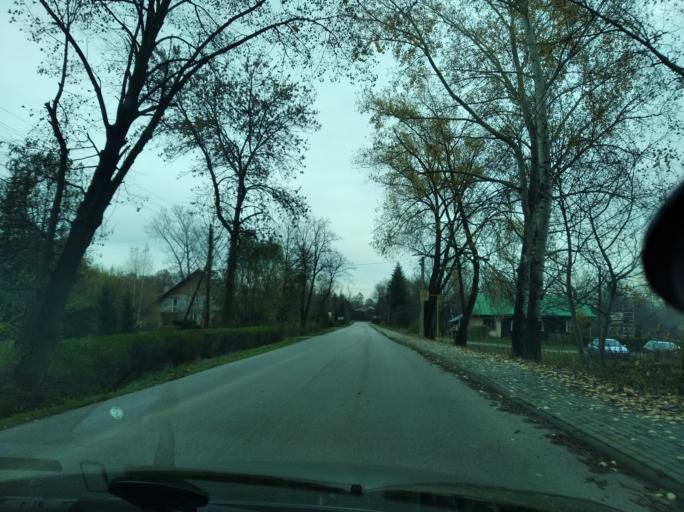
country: PL
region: Subcarpathian Voivodeship
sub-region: Powiat przeworski
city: Gac
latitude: 50.0267
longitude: 22.3454
